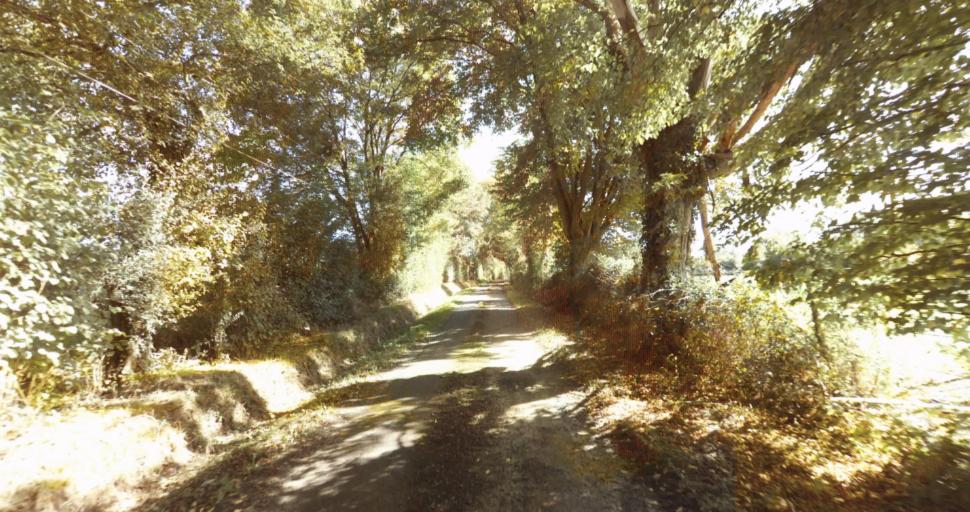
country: FR
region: Lower Normandy
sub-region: Departement de l'Orne
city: Gace
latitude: 48.7277
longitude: 0.2417
